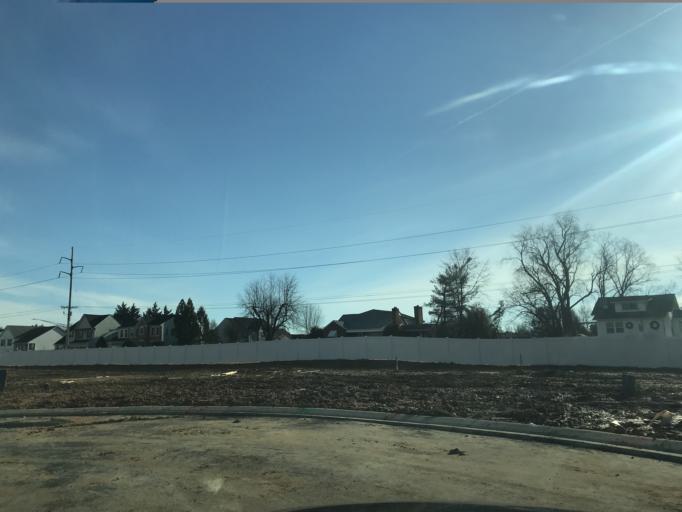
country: US
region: Maryland
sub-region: Baltimore County
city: Middle River
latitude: 39.3570
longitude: -76.4322
